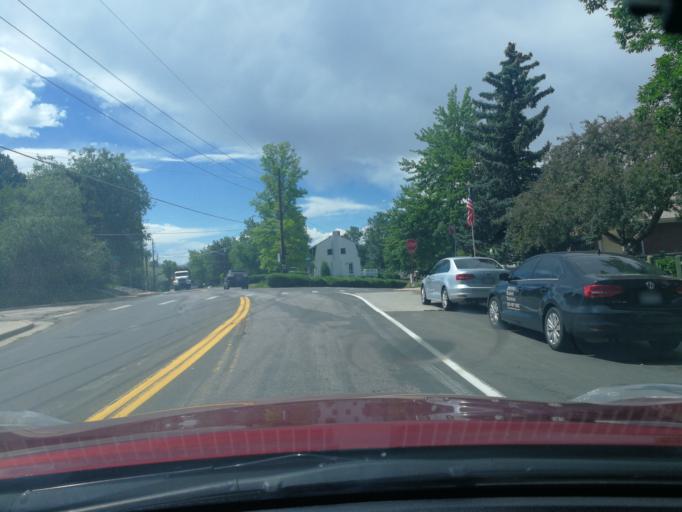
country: US
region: Colorado
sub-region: Arapahoe County
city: Littleton
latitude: 39.5936
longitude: -105.0019
